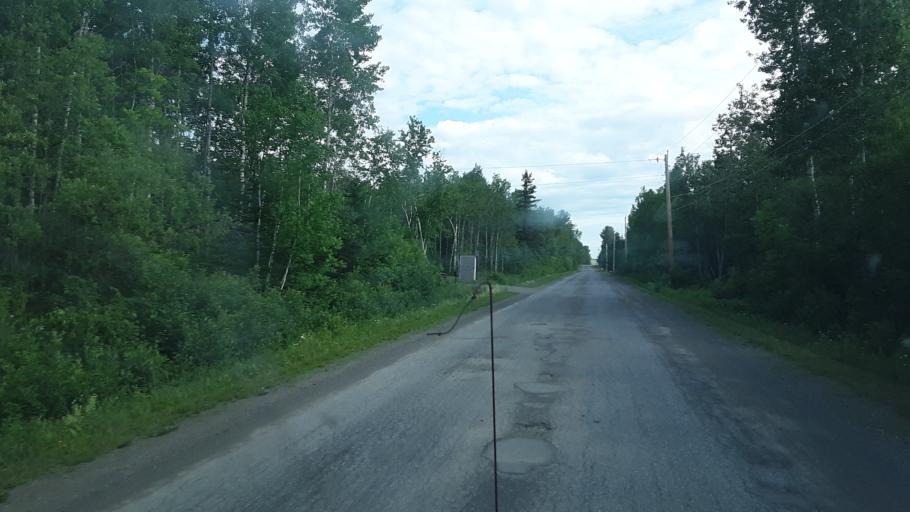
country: US
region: Maine
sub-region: Aroostook County
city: Caribou
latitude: 46.8457
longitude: -68.0917
